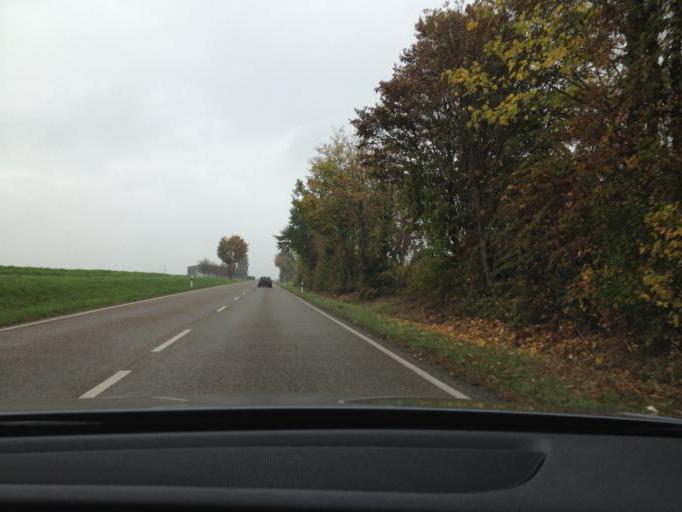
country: DE
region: Baden-Wuerttemberg
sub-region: Regierungsbezirk Stuttgart
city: Bad Wimpfen
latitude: 49.2266
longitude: 9.1457
